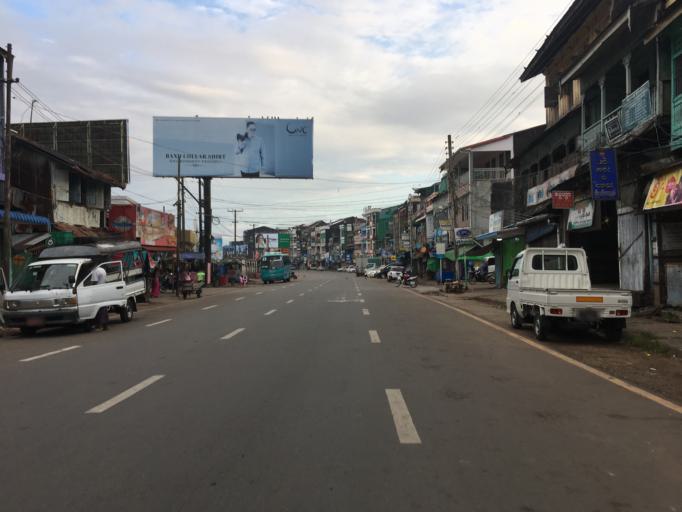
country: MM
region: Mon
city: Mawlamyine
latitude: 16.4926
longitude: 97.6186
